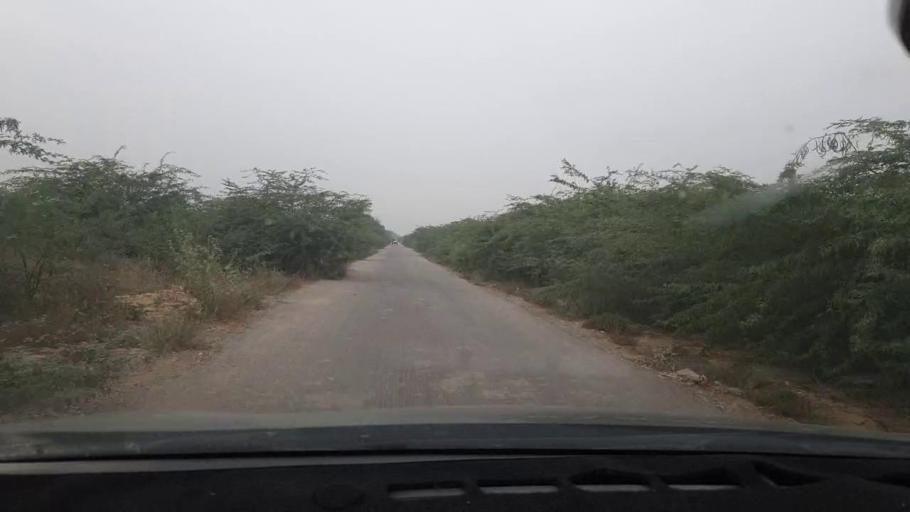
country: PK
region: Sindh
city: Malir Cantonment
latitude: 24.9253
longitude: 67.3272
